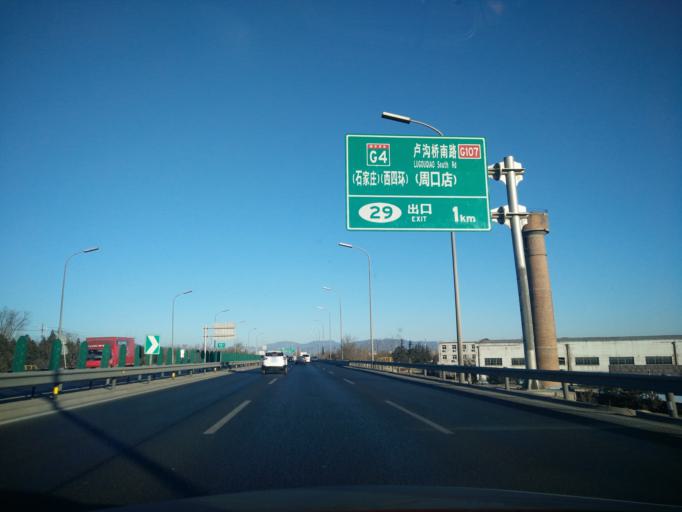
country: CN
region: Beijing
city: Fengtai
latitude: 39.8346
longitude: 116.2284
